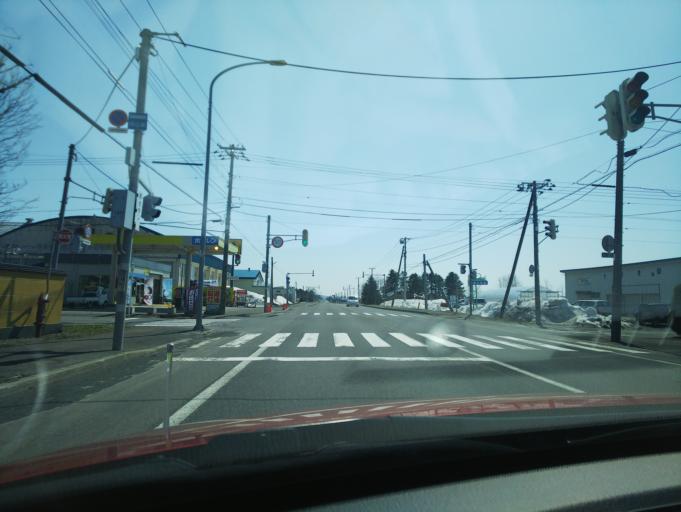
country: JP
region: Hokkaido
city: Nayoro
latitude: 44.2361
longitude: 142.3948
